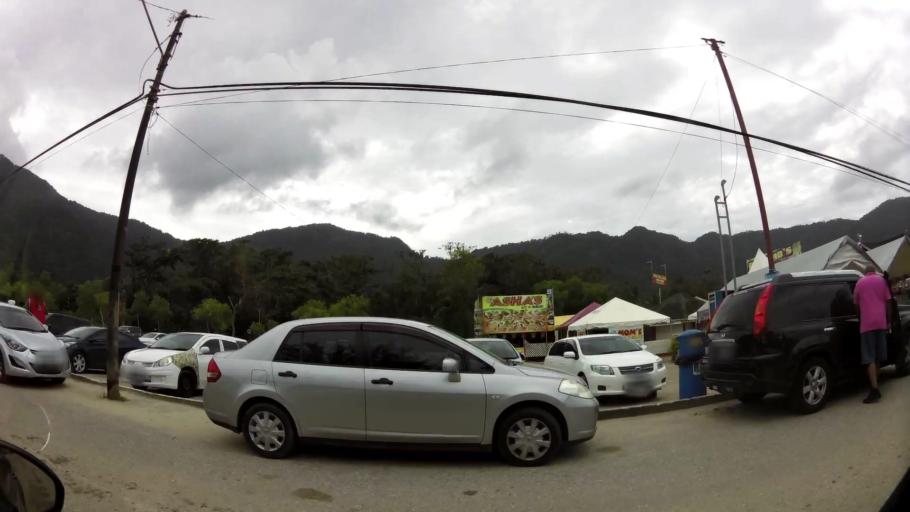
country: TT
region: Diego Martin
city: Petit Valley
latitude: 10.7580
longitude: -61.4389
